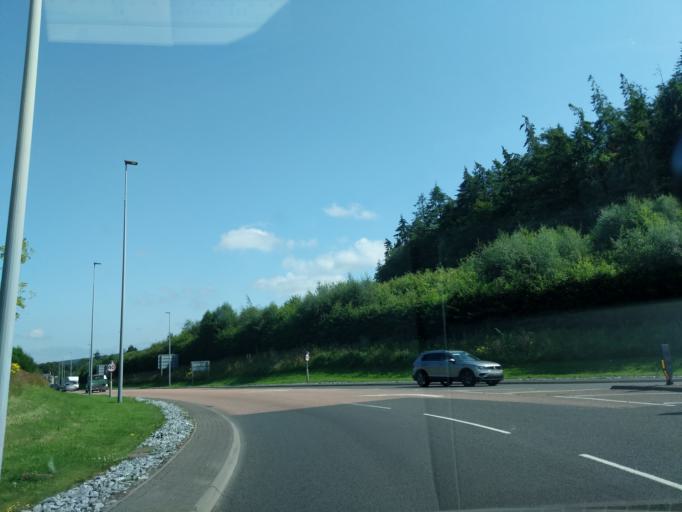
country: GB
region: Scotland
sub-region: Moray
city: Fochabers
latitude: 57.6228
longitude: -3.1144
